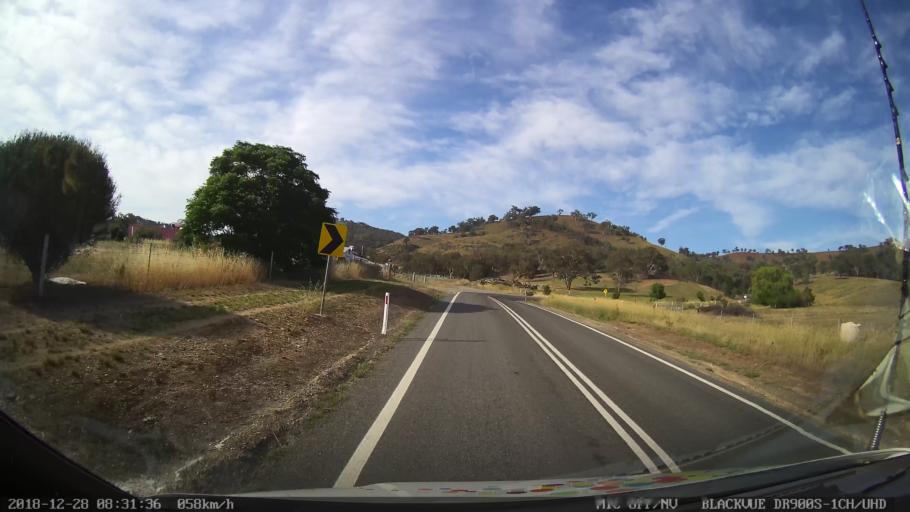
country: AU
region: New South Wales
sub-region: Blayney
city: Blayney
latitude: -33.9603
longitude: 149.3177
